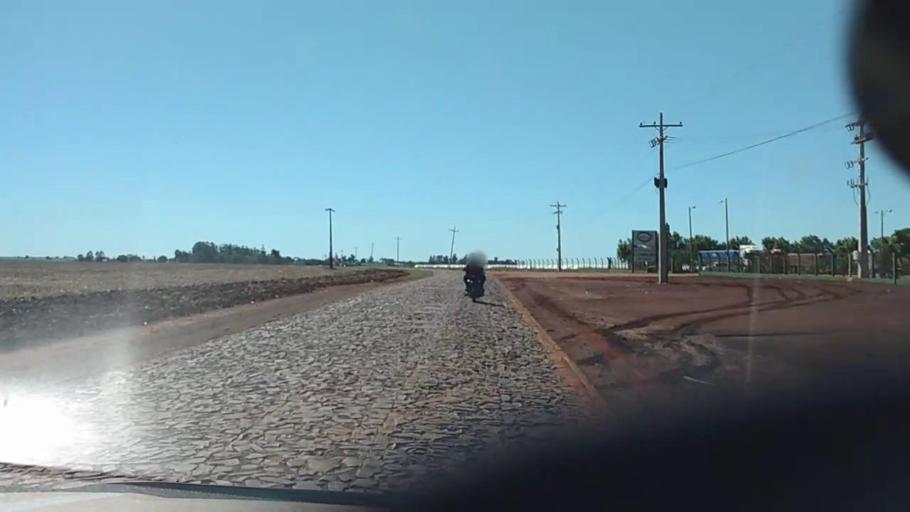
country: PY
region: Alto Parana
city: Naranjal
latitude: -25.9704
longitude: -55.1505
